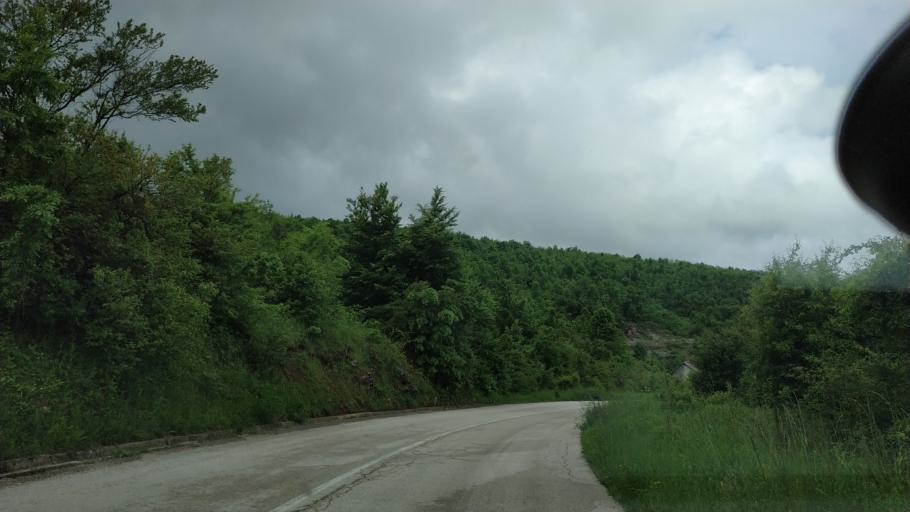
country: RS
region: Central Serbia
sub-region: Zajecarski Okrug
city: Boljevac
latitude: 43.7279
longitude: 21.9515
